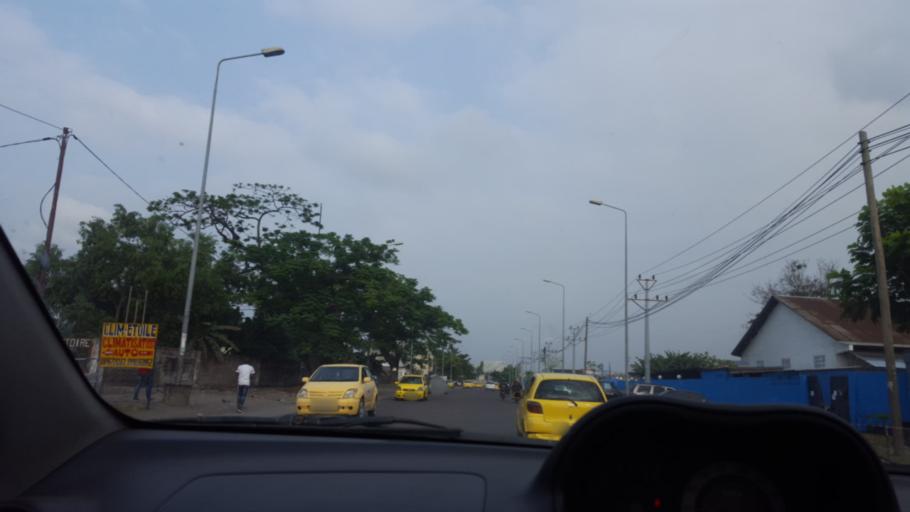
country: CD
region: Kinshasa
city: Kinshasa
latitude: -4.3377
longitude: 15.3040
